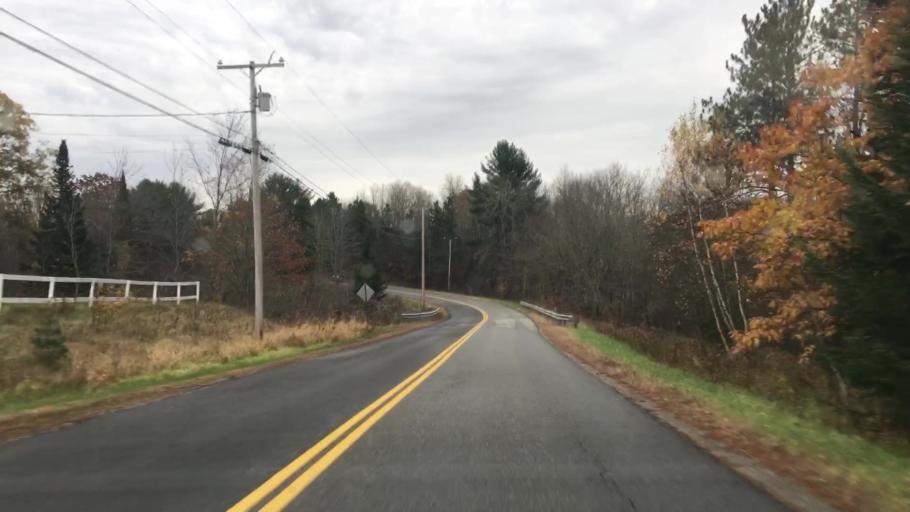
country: US
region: Maine
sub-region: Lincoln County
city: Whitefield
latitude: 44.1666
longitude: -69.6903
